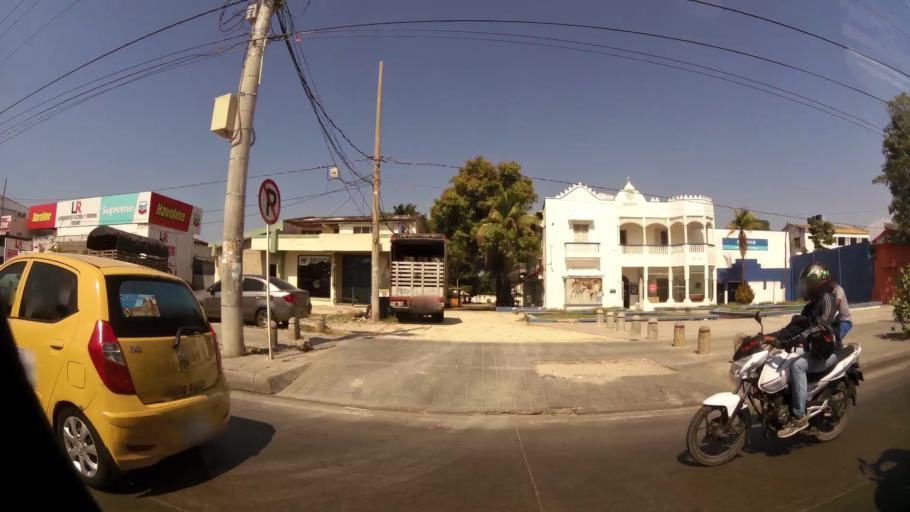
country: CO
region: Bolivar
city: Cartagena
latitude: 10.4103
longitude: -75.5179
